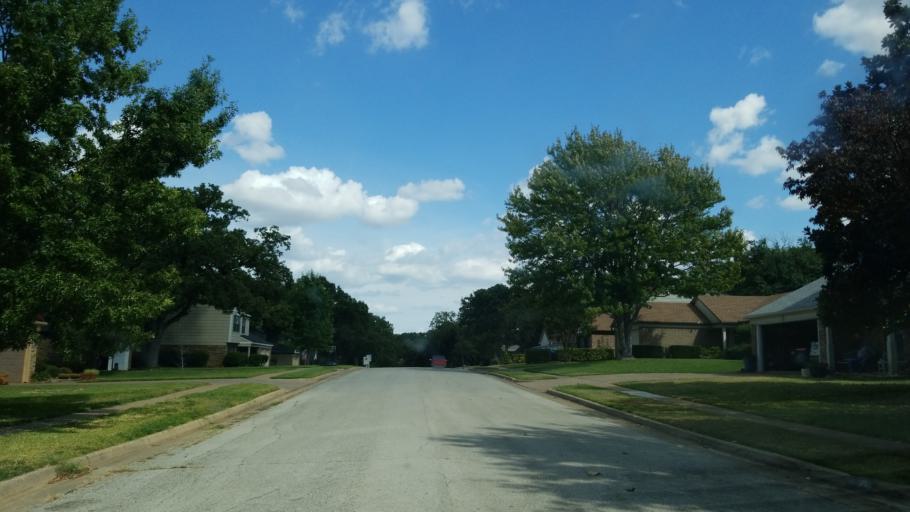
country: US
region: Texas
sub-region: Tarrant County
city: Euless
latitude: 32.8608
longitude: -97.0776
